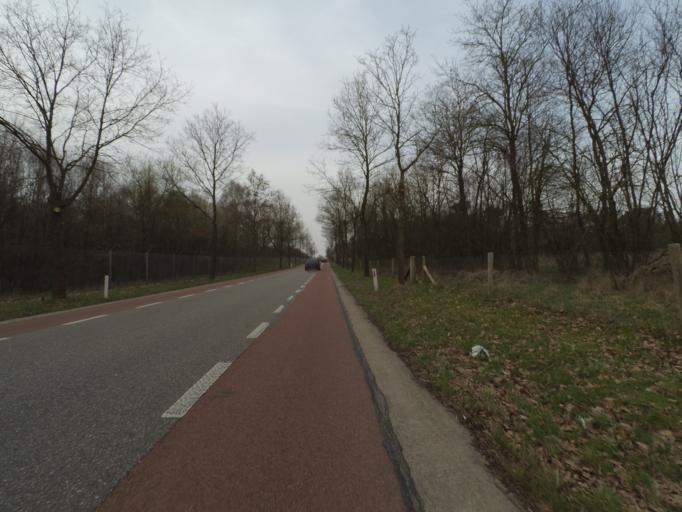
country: NL
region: Gelderland
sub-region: Gemeente Arnhem
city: Gulden Bodem
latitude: 52.0469
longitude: 5.9012
